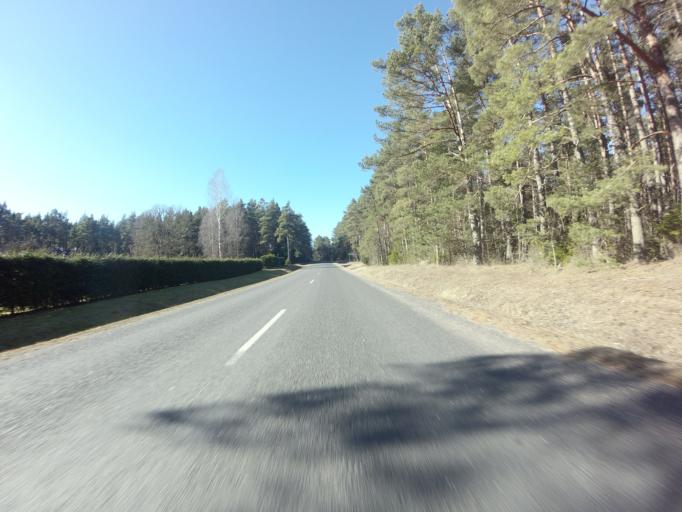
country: EE
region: Saare
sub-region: Kuressaare linn
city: Kuressaare
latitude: 58.5885
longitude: 22.6128
